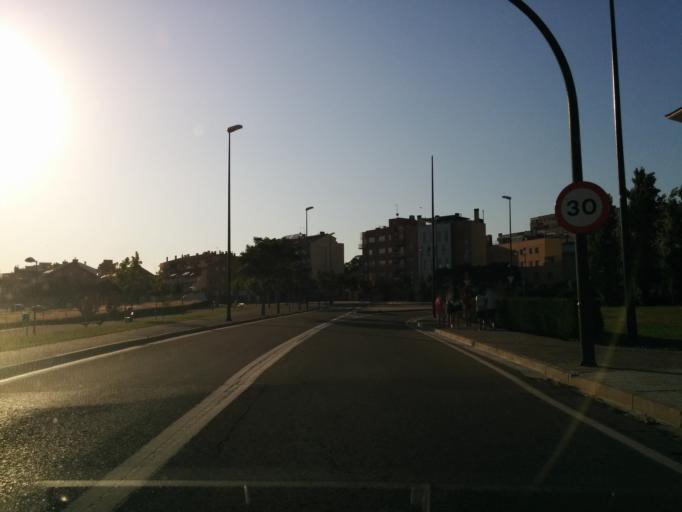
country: ES
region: Aragon
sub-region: Provincia de Zaragoza
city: Zaragoza
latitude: 41.6656
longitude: -0.8242
